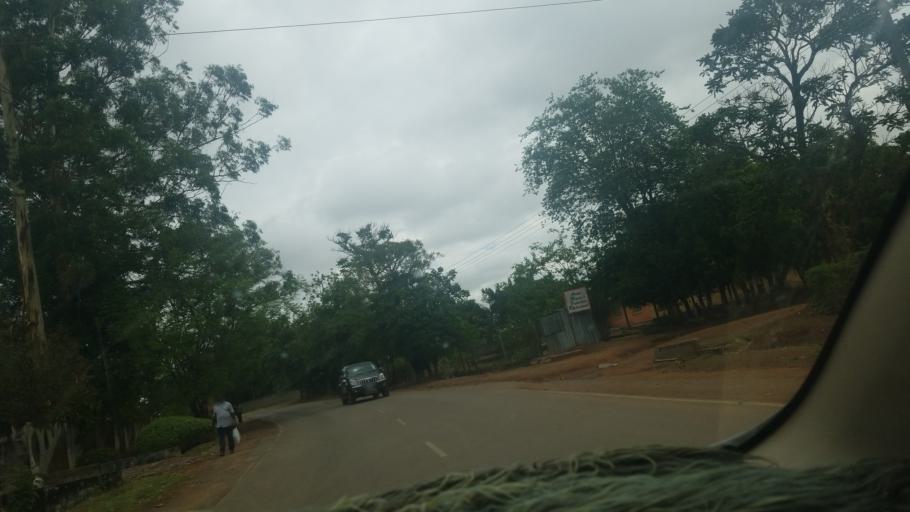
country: ZM
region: Luapula
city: Mansa
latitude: -11.1974
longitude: 28.8924
